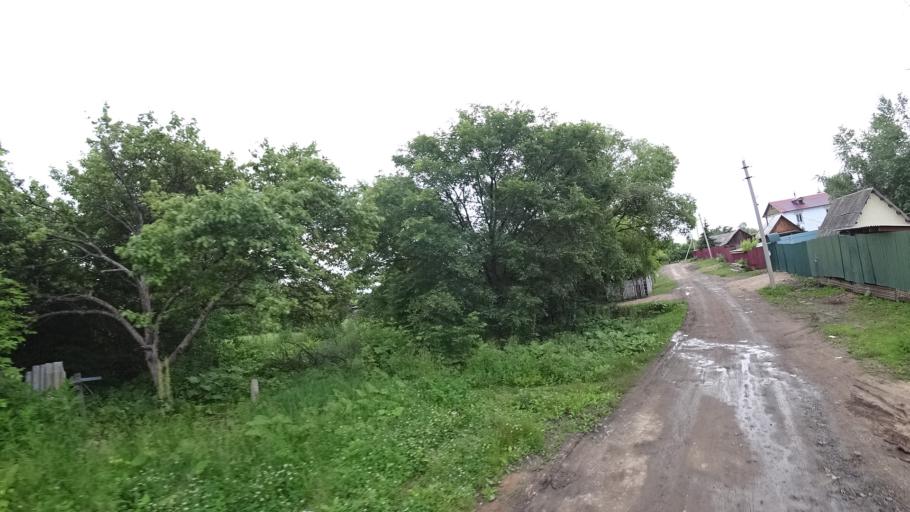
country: RU
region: Primorskiy
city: Novosysoyevka
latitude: 44.2244
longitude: 133.3543
